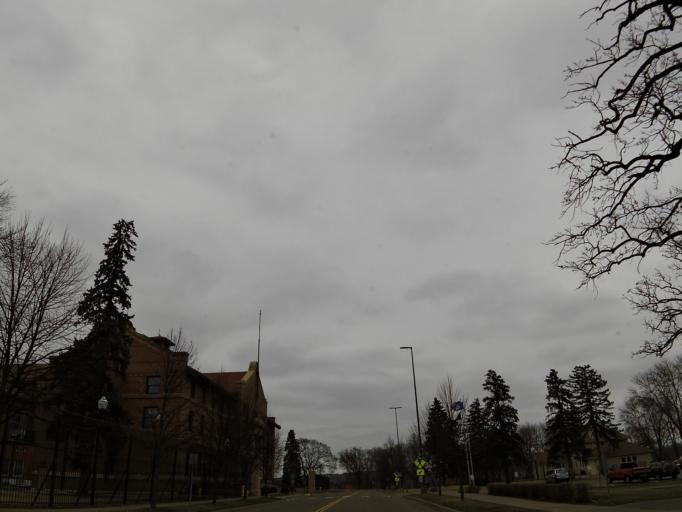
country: US
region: Minnesota
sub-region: Washington County
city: Oak Park Heights
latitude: 45.0271
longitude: -92.7868
